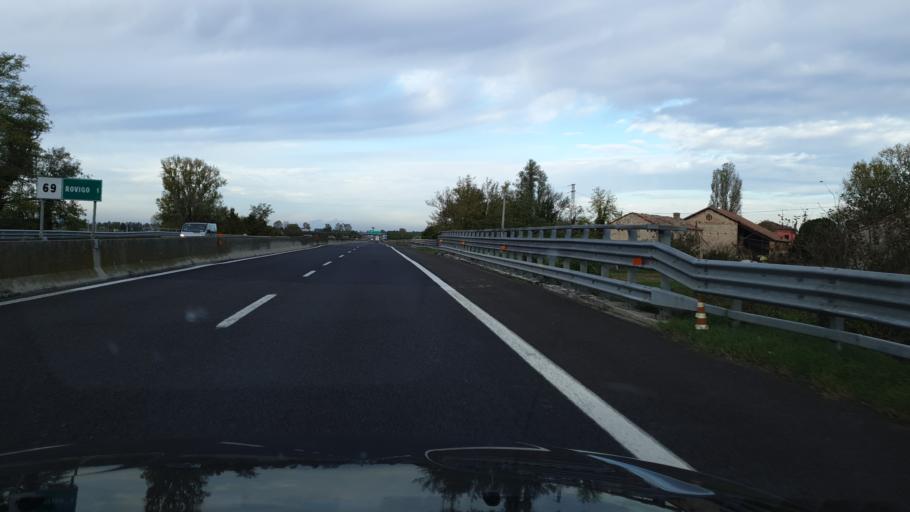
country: IT
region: Veneto
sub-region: Provincia di Rovigo
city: Grignano Polesine
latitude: 45.0713
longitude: 11.7335
